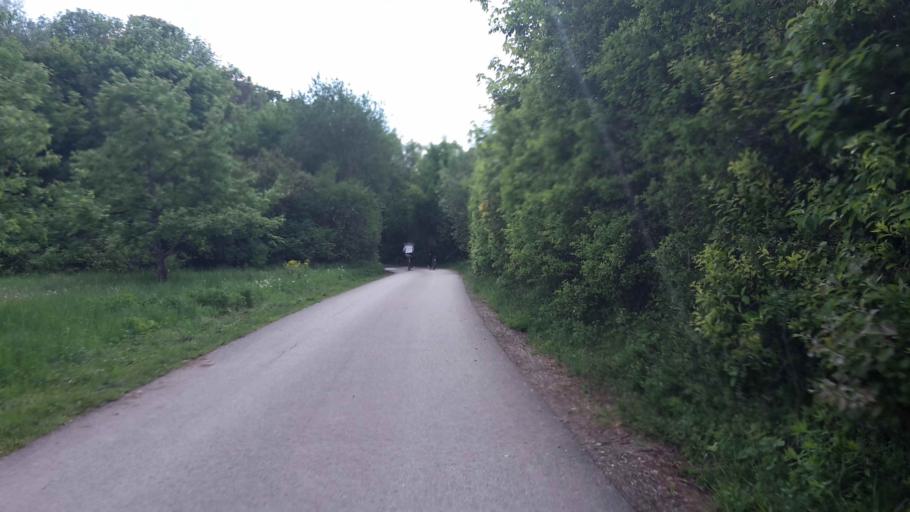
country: DE
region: Bavaria
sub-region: Upper Bavaria
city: Karlsfeld
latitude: 48.1915
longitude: 11.4813
